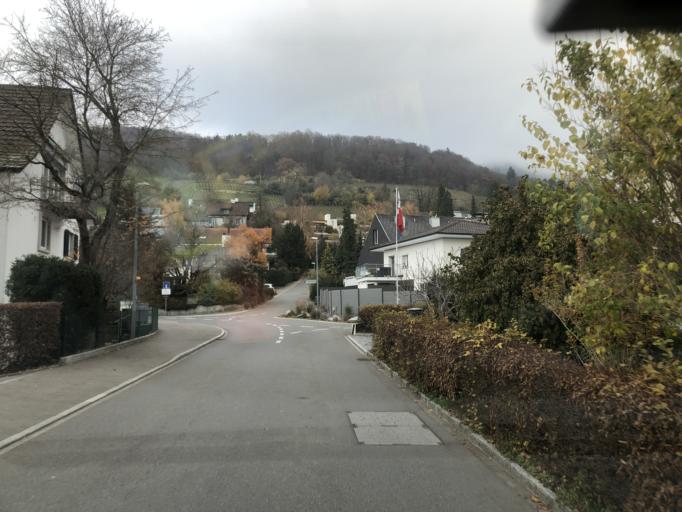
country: CH
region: Aargau
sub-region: Bezirk Baden
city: Wettingen
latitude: 47.4689
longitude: 8.3301
